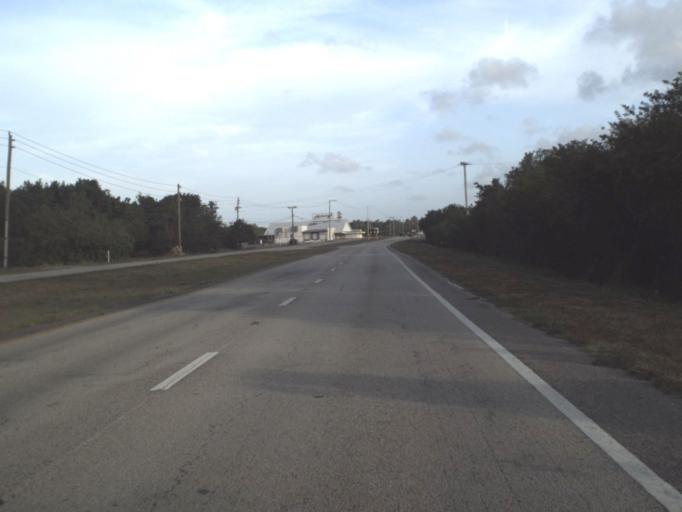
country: US
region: Florida
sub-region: Brevard County
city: Rockledge
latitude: 28.3008
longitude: -80.7030
